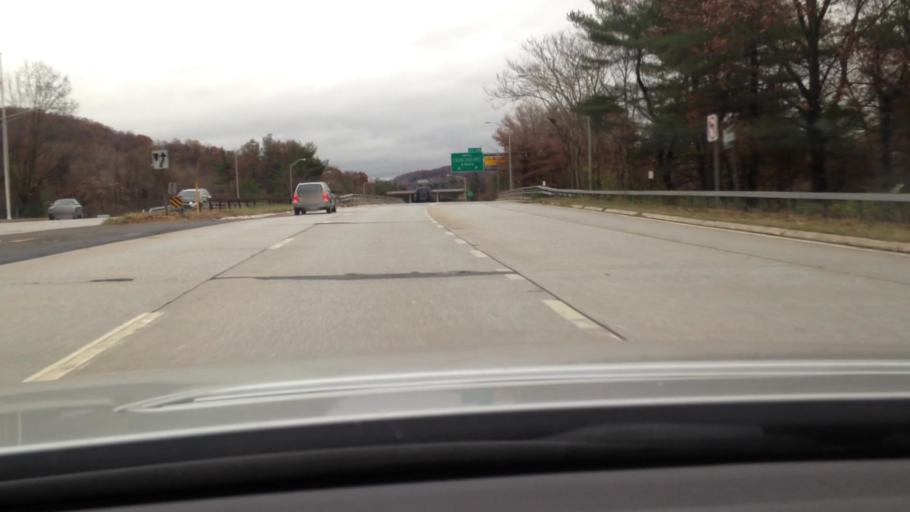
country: US
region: New York
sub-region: Westchester County
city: Hawthorne
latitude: 41.1075
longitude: -73.8076
